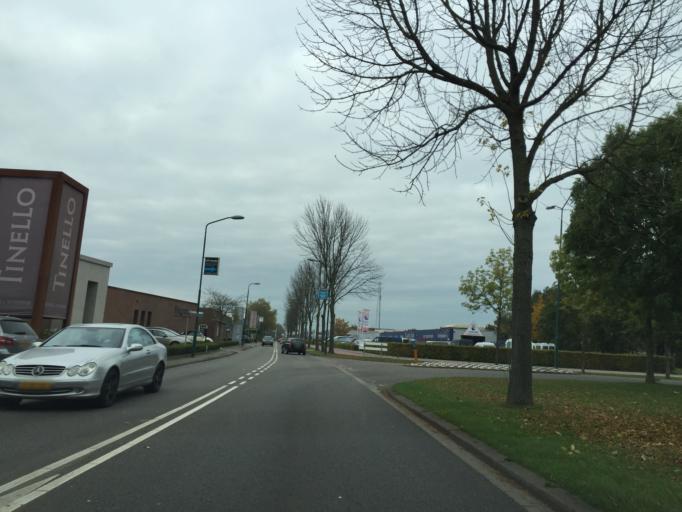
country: NL
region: North Brabant
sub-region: Gemeente Waalwijk
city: Waalwijk
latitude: 51.6651
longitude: 5.0355
